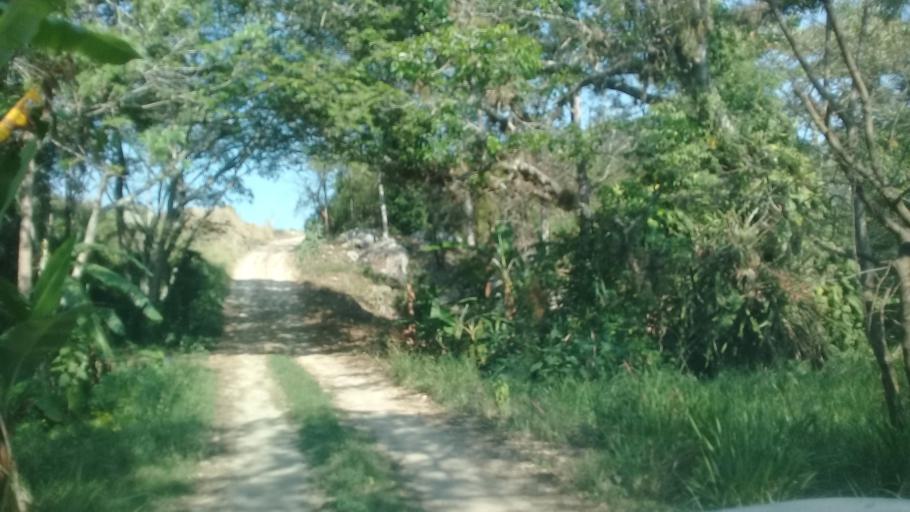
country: MX
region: Veracruz
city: El Castillo
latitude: 19.5728
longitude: -96.8376
